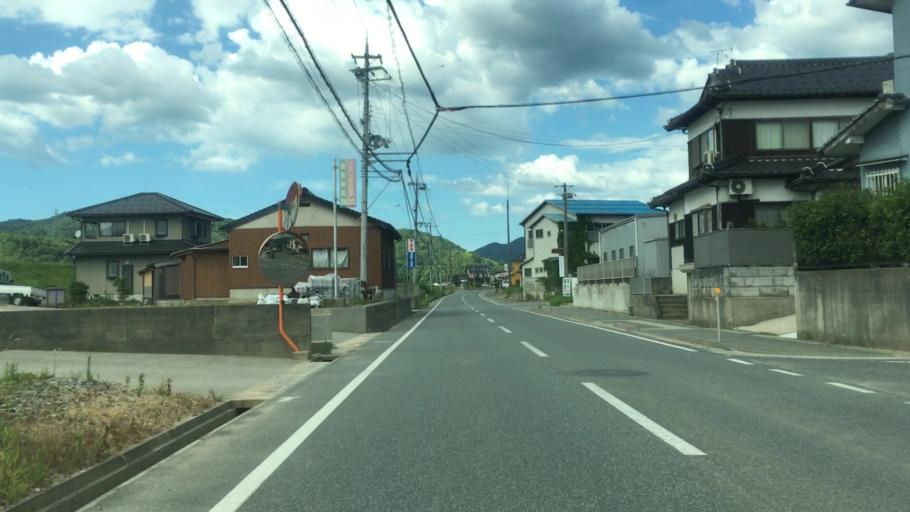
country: JP
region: Hyogo
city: Toyooka
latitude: 35.5534
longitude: 134.7931
